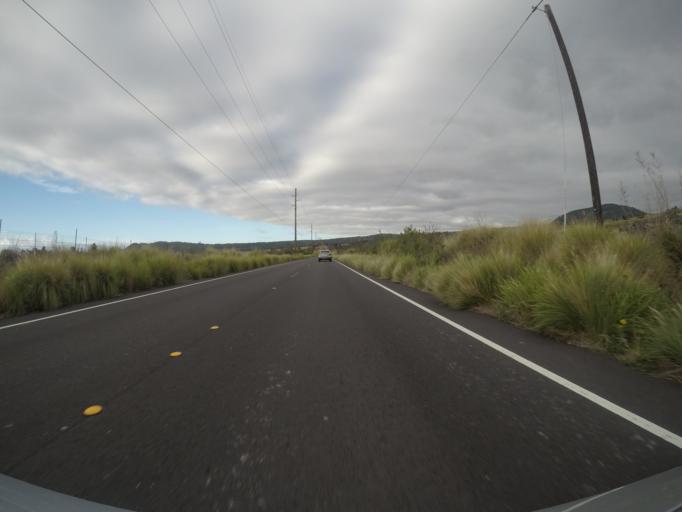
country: US
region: Hawaii
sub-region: Hawaii County
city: Kalaoa
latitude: 19.7932
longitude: -155.8723
